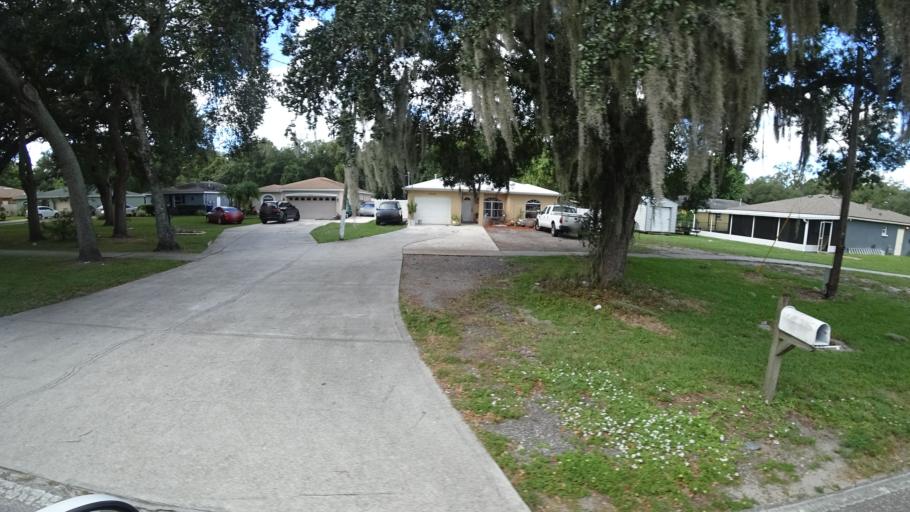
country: US
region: Florida
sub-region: Manatee County
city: West Samoset
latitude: 27.4747
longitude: -82.5548
